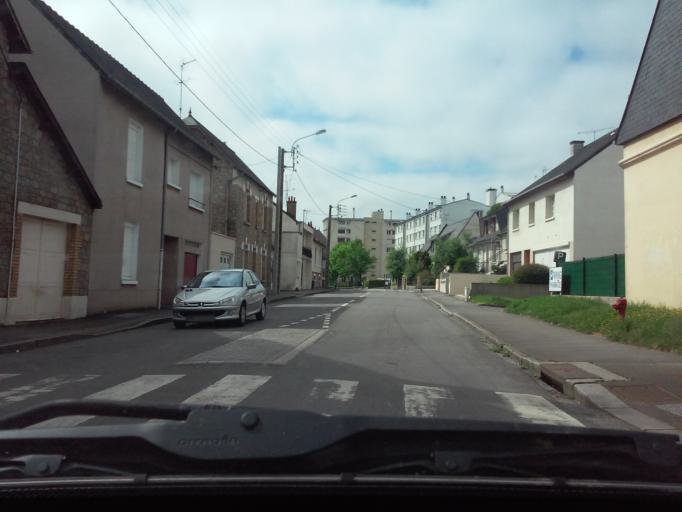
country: FR
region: Brittany
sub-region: Departement d'Ille-et-Vilaine
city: Rennes
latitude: 48.0944
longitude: -1.6856
